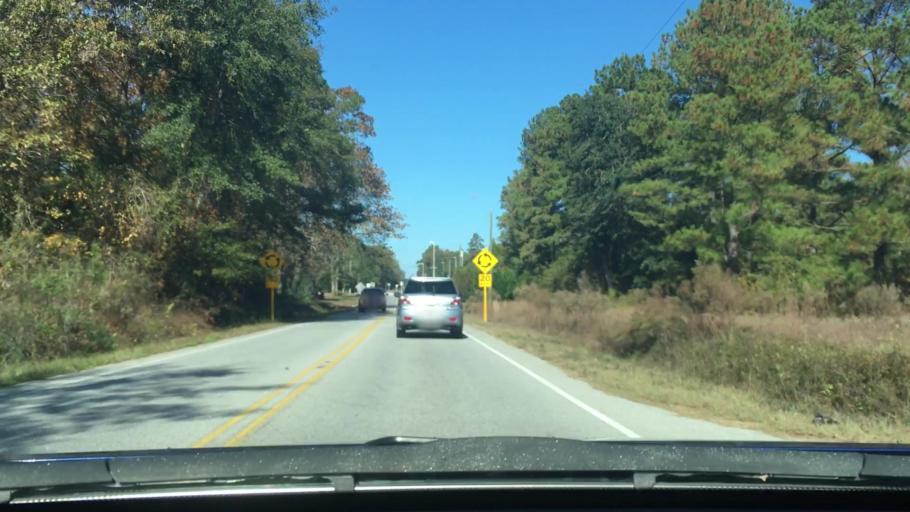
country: US
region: South Carolina
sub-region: Sumter County
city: South Sumter
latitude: 33.8865
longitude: -80.3641
